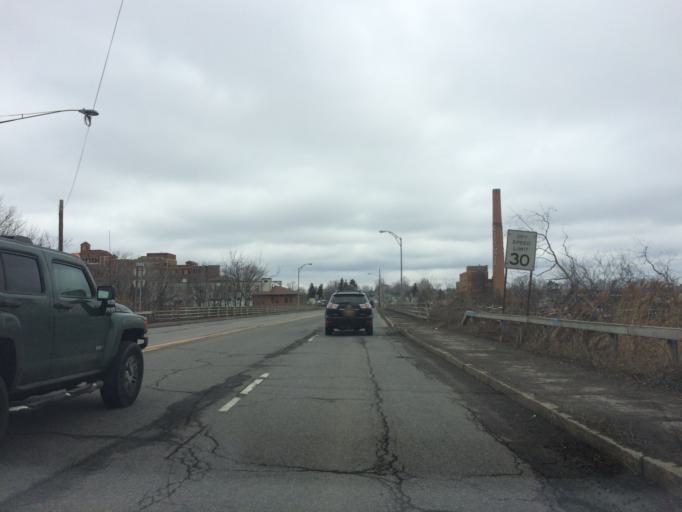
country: US
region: New York
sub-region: Monroe County
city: Rochester
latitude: 43.1095
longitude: -77.6159
